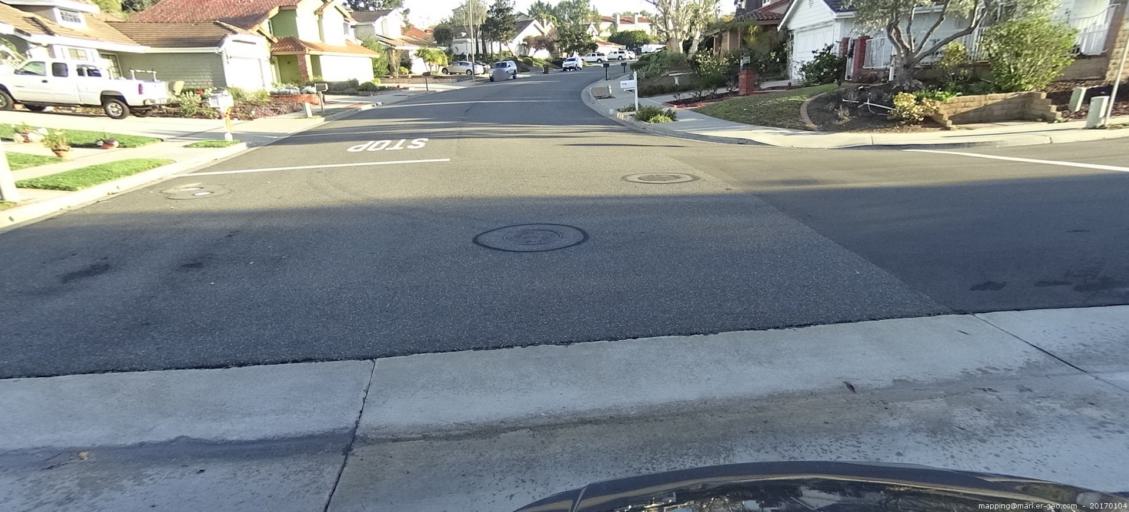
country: US
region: California
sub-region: Orange County
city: Dana Point
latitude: 33.4857
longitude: -117.7035
